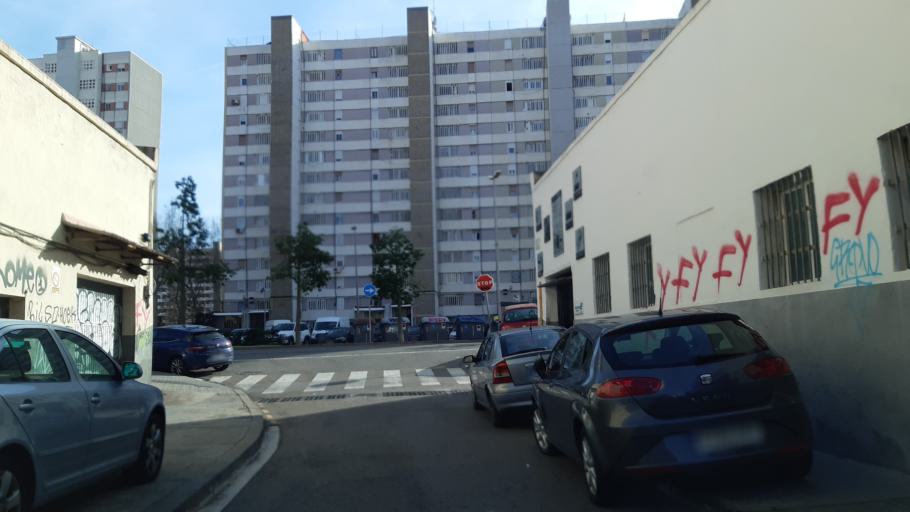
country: ES
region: Catalonia
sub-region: Provincia de Barcelona
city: L'Hospitalet de Llobregat
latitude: 41.3552
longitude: 2.1093
